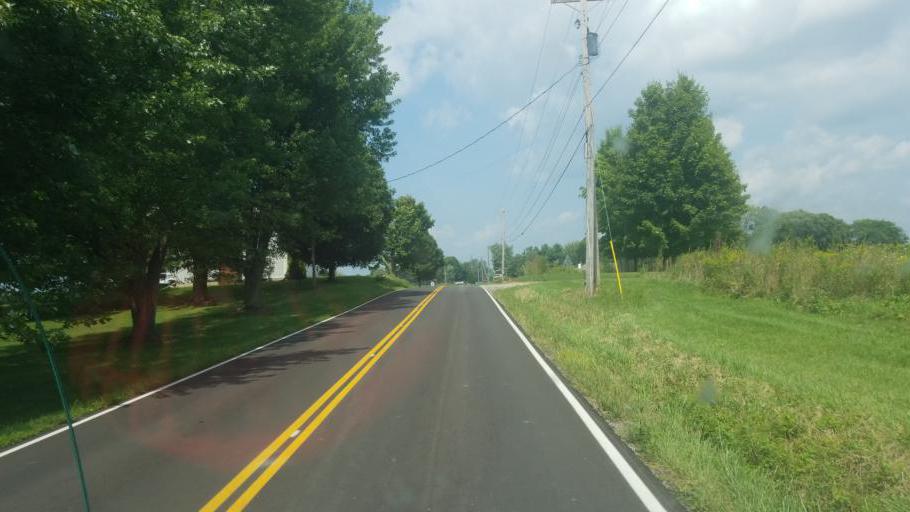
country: US
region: Ohio
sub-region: Richland County
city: Shelby
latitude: 40.8475
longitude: -82.6294
